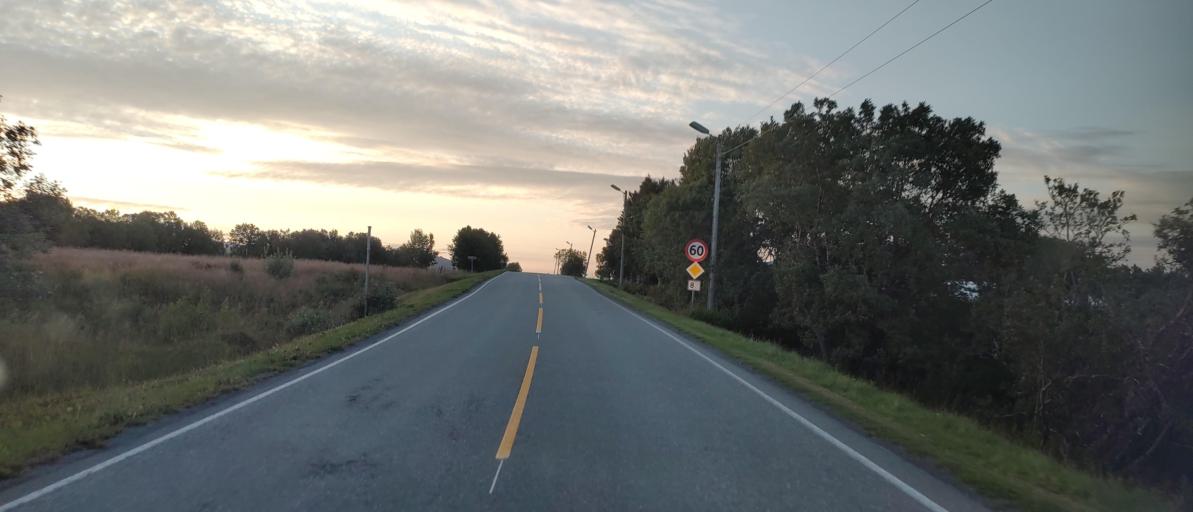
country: NO
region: Nordland
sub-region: Andoy
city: Andenes
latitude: 69.2453
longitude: 16.1180
